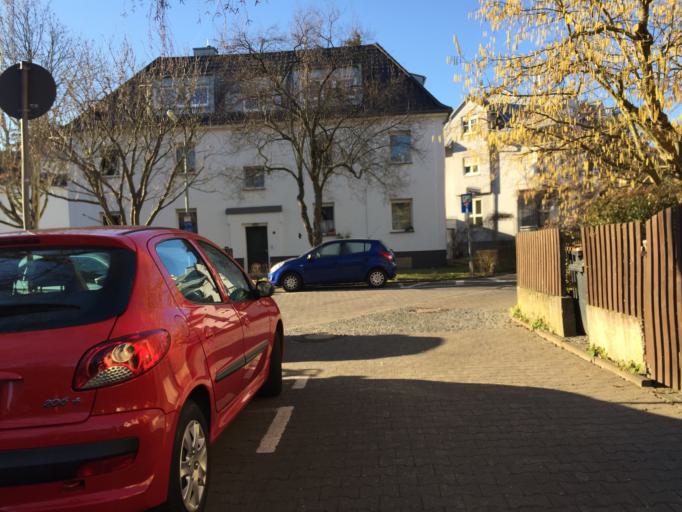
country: DE
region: Hesse
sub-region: Regierungsbezirk Darmstadt
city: Frankfurt am Main
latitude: 50.1558
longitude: 8.6689
